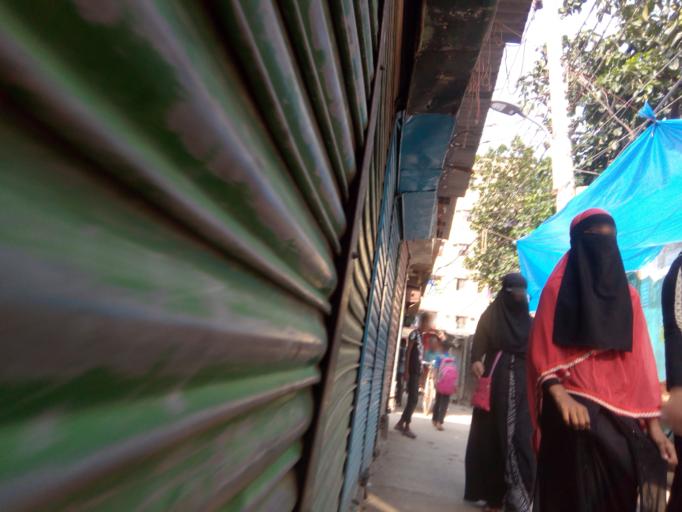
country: BD
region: Dhaka
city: Azimpur
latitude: 23.7090
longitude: 90.3807
